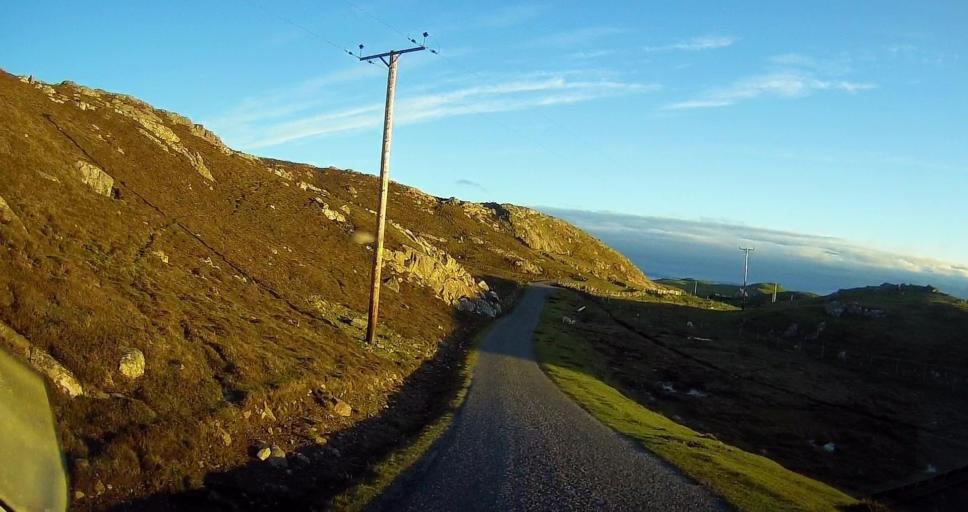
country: GB
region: Scotland
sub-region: Shetland Islands
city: Lerwick
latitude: 60.4450
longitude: -1.4412
